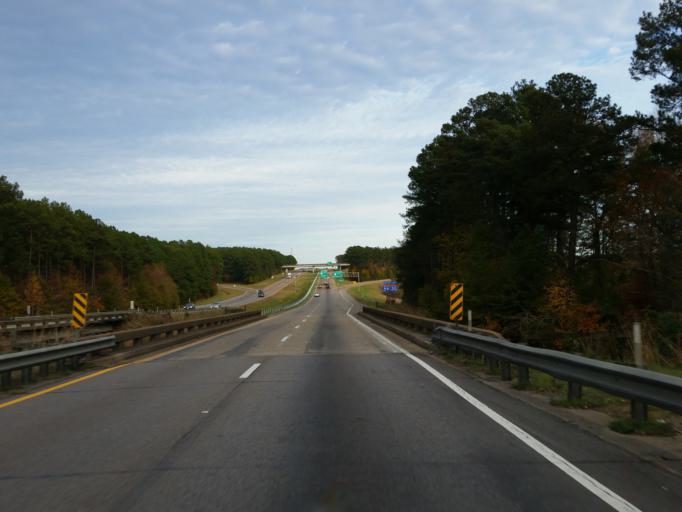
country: US
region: Mississippi
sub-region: Lauderdale County
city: Marion
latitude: 32.3815
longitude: -88.6455
